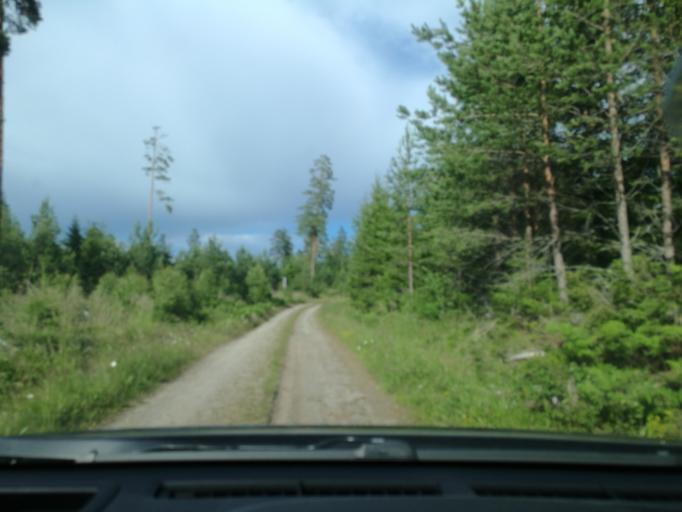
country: SE
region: Vaestmanland
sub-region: Surahammars Kommun
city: Ramnas
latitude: 59.8318
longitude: 16.2420
